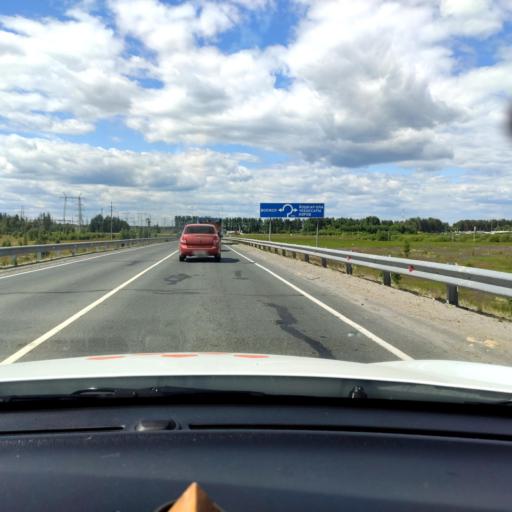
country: RU
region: Mariy-El
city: Volzhsk
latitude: 55.9091
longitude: 48.3726
